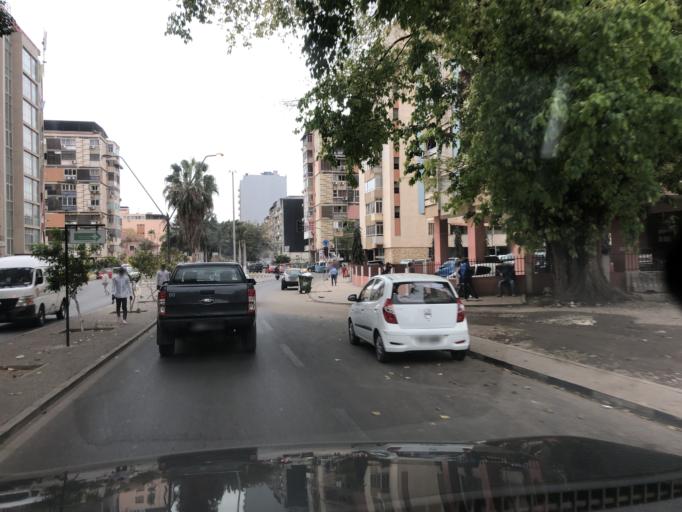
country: AO
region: Luanda
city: Luanda
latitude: -8.8300
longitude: 13.2306
